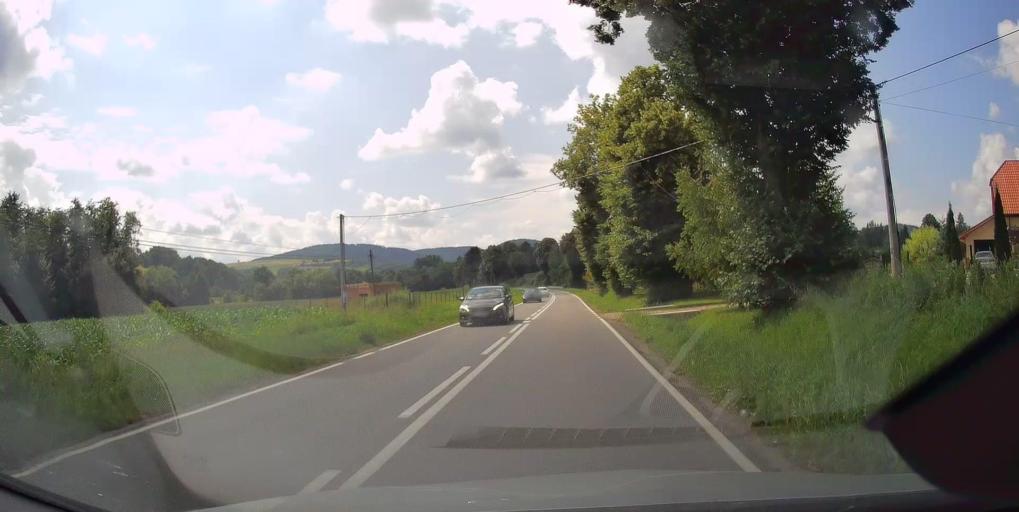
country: PL
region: Lesser Poland Voivodeship
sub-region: Powiat tarnowski
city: Zakliczyn
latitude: 49.8444
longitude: 20.8091
